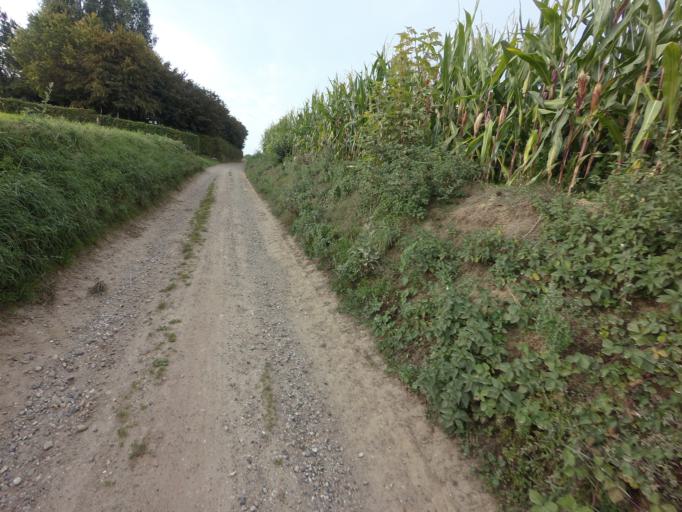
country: NL
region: Limburg
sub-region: Eijsden-Margraten
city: Margraten
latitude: 50.8261
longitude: 5.8375
